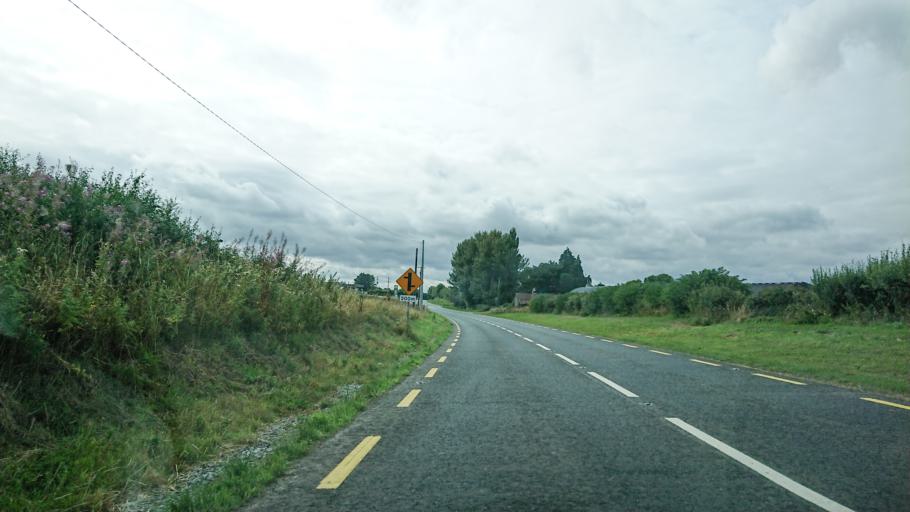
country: IE
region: Munster
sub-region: County Cork
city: Mallow
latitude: 52.1557
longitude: -8.4999
